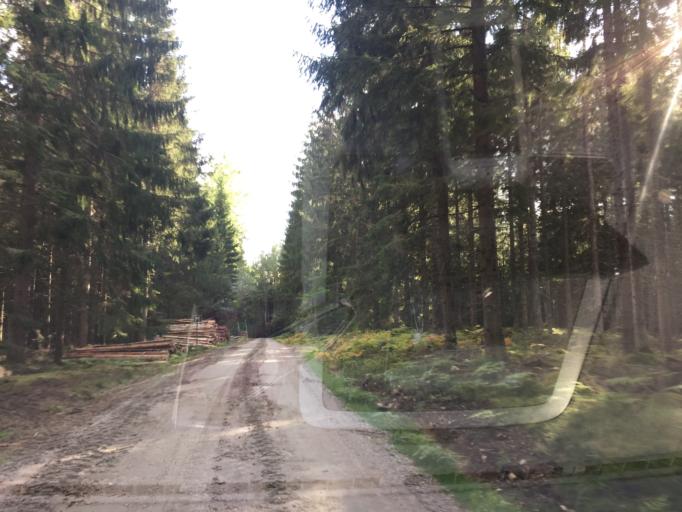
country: SE
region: Soedermanland
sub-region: Vingakers Kommun
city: Vingaker
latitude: 59.0002
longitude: 15.7403
